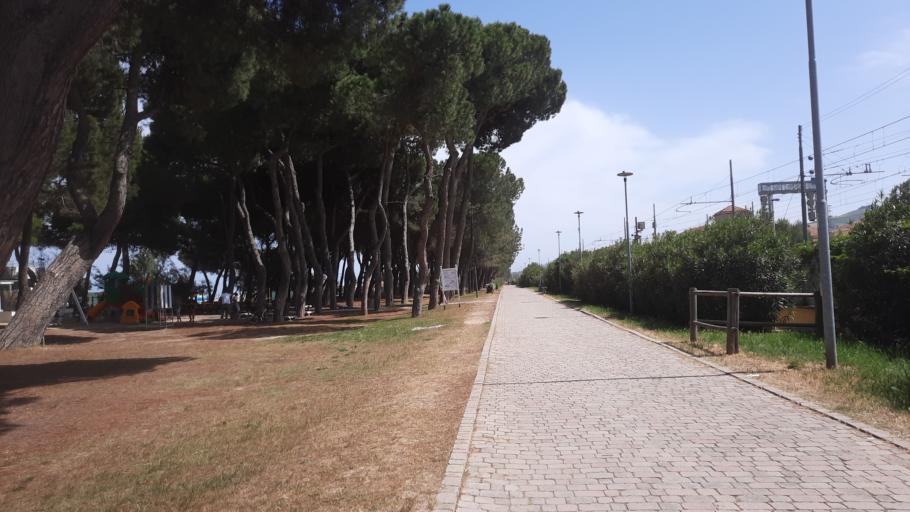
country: IT
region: Abruzzo
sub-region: Provincia di Teramo
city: Pineto
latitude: 42.6098
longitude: 14.0678
